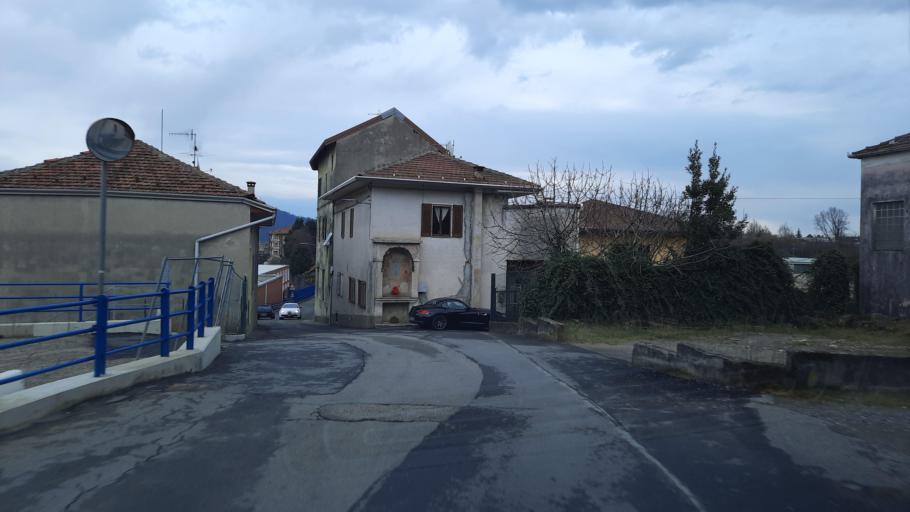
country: IT
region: Piedmont
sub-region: Provincia di Novara
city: San Maurizio D'Opaglio
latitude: 45.7710
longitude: 8.3930
